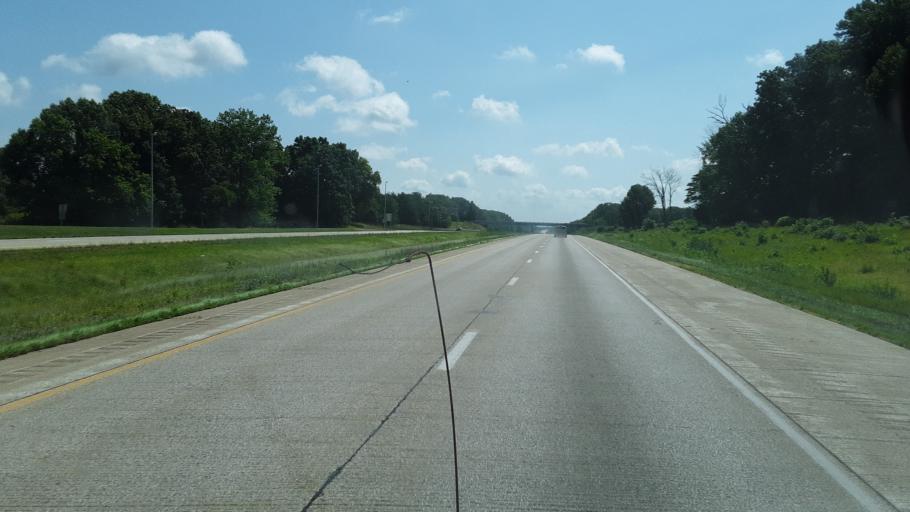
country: US
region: Illinois
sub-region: Clark County
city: Marshall
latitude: 39.4217
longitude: -87.6591
